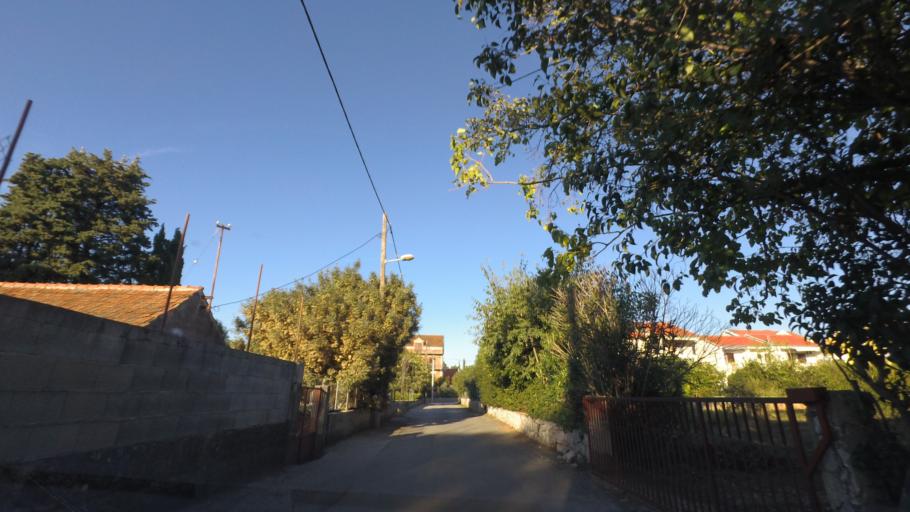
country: HR
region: Zadarska
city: Biograd na Moru
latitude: 43.9406
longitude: 15.4500
